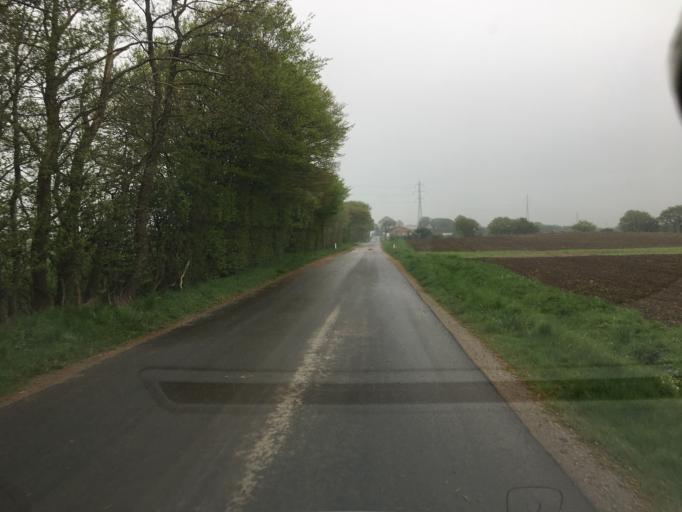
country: DK
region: South Denmark
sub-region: Haderslev Kommune
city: Haderslev
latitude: 55.2751
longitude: 9.4319
